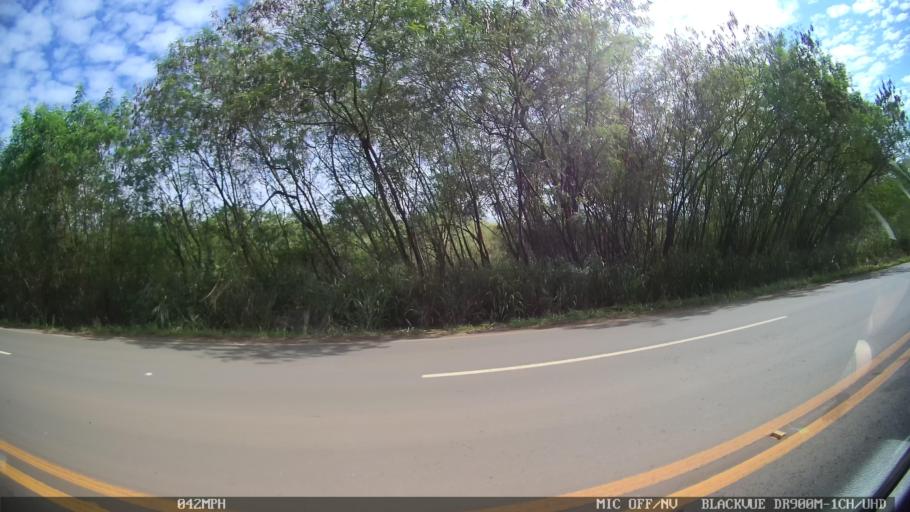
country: BR
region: Sao Paulo
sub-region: Santa Barbara D'Oeste
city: Santa Barbara d'Oeste
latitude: -22.7123
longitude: -47.4279
